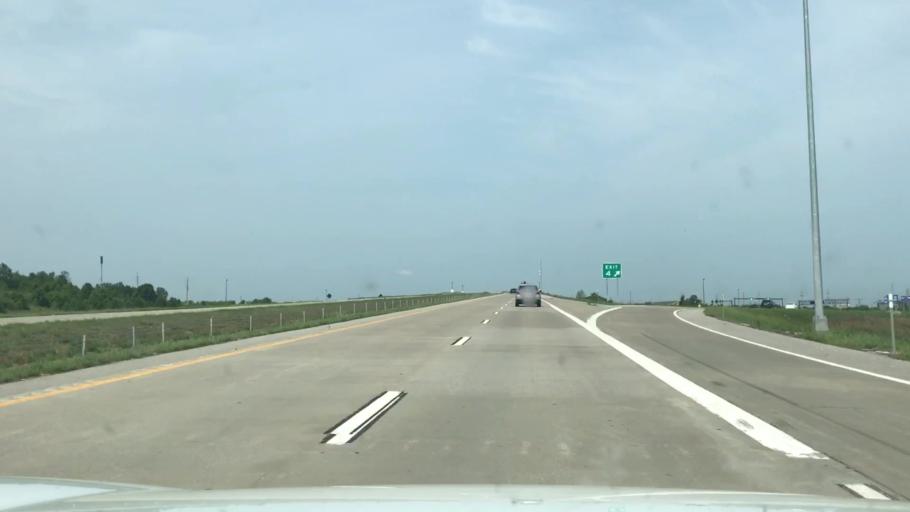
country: US
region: Missouri
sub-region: Saint Charles County
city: Dardenne Prairie
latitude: 38.7523
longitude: -90.6958
